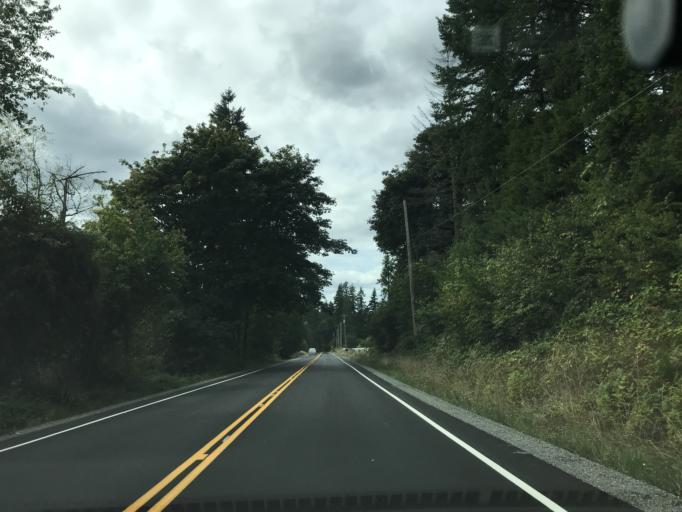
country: US
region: Washington
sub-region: King County
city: Black Diamond
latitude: 47.2867
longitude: -122.0156
